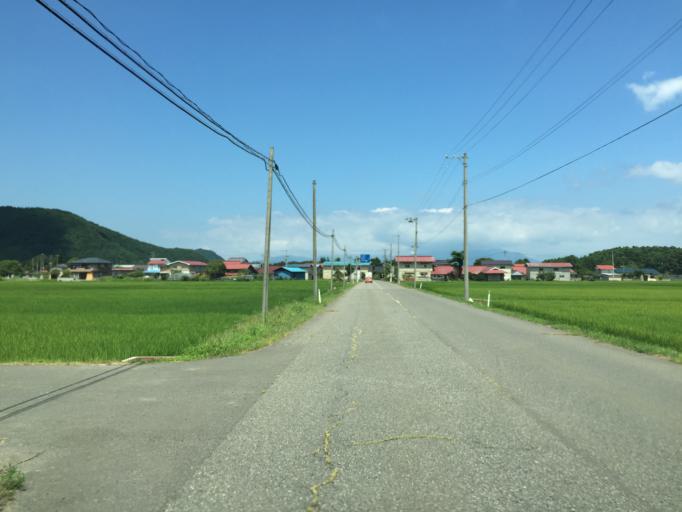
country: JP
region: Fukushima
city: Inawashiro
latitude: 37.4130
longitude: 140.0851
